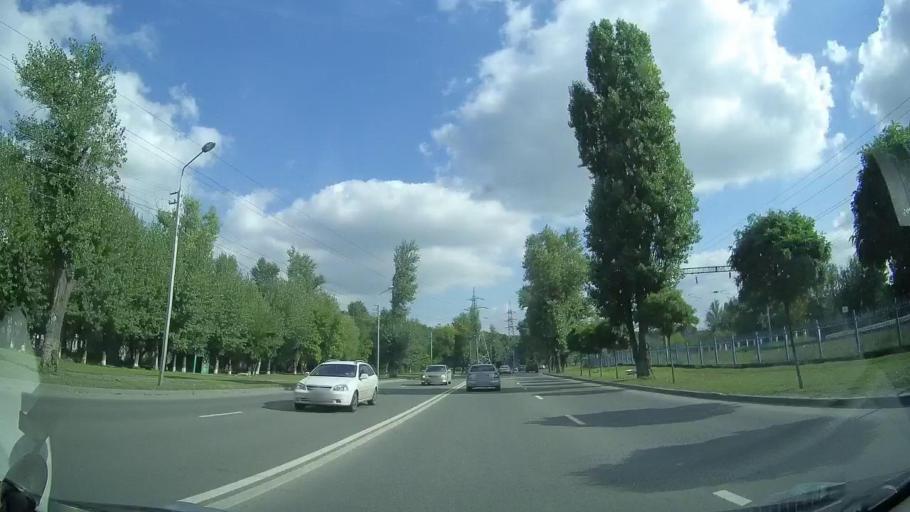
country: RU
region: Rostov
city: Imeni Chkalova
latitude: 47.2599
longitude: 39.7889
